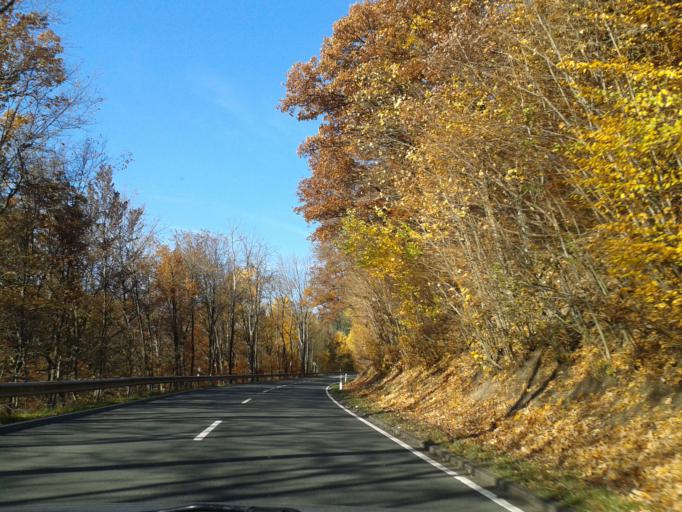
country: DE
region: North Rhine-Westphalia
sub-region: Regierungsbezirk Arnsberg
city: Bad Laasphe
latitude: 50.9516
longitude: 8.3587
